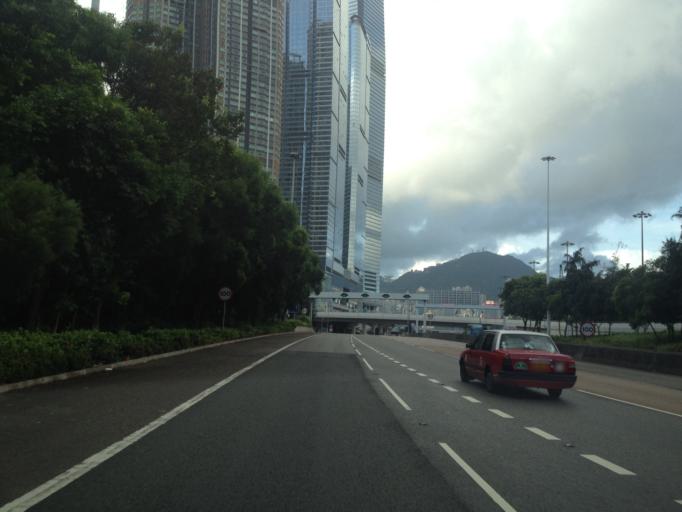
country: HK
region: Sham Shui Po
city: Sham Shui Po
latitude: 22.3098
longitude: 114.1617
